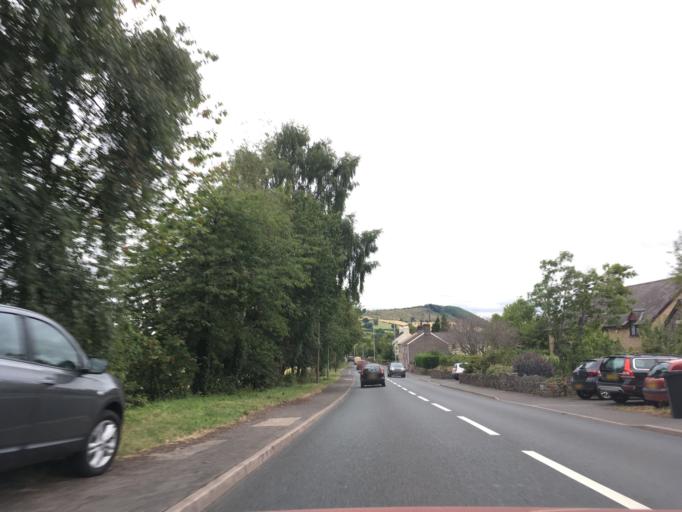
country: GB
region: Wales
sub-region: Blaenau Gwent
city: Brynmawr
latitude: 51.8927
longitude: -3.2423
